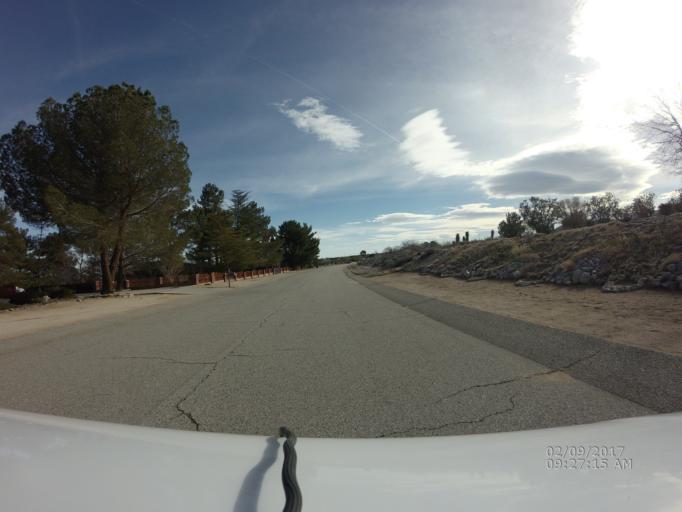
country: US
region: California
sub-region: Los Angeles County
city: Lake Los Angeles
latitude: 34.4726
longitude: -117.8392
